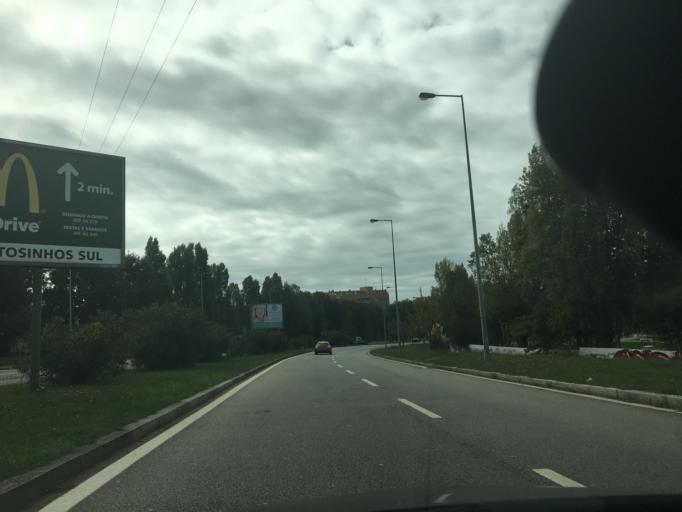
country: PT
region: Porto
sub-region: Matosinhos
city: Matosinhos
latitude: 41.1821
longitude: -8.6777
